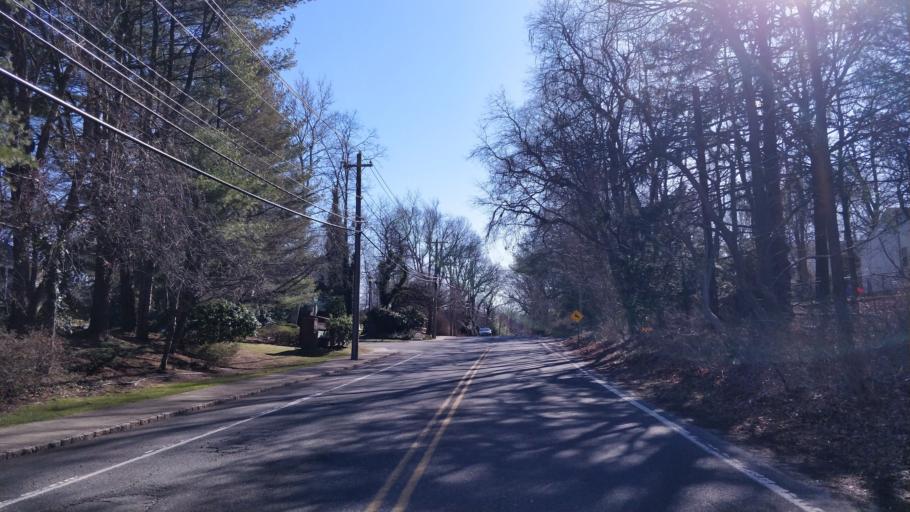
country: US
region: New York
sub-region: Suffolk County
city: Setauket-East Setauket
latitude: 40.9081
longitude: -73.1013
